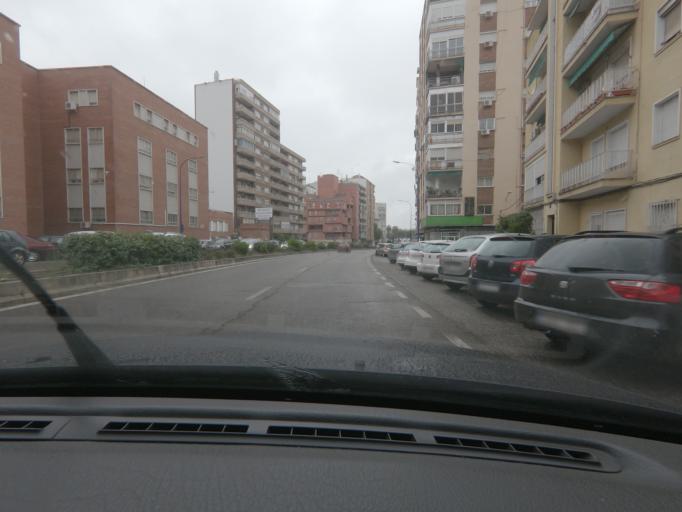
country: ES
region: Extremadura
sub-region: Provincia de Badajoz
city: Badajoz
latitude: 38.8694
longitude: -6.9759
